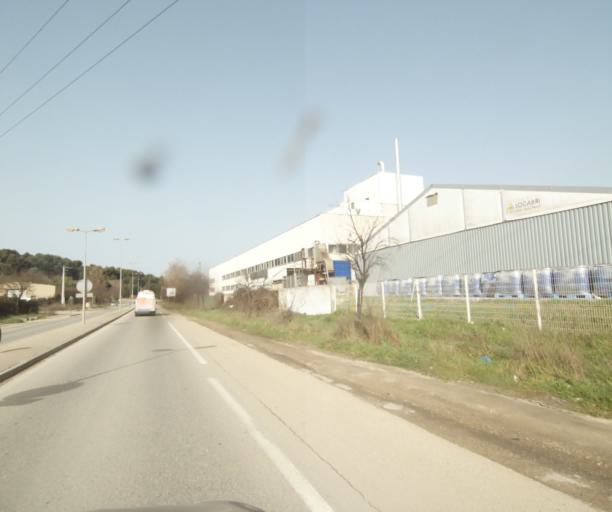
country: FR
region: Provence-Alpes-Cote d'Azur
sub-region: Departement des Bouches-du-Rhone
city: Gardanne
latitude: 43.4664
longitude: 5.4822
